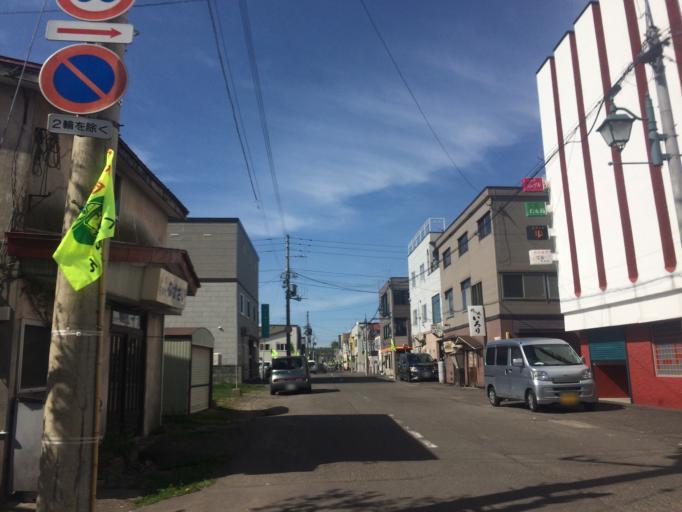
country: JP
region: Hokkaido
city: Niseko Town
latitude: 42.9018
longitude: 140.7512
